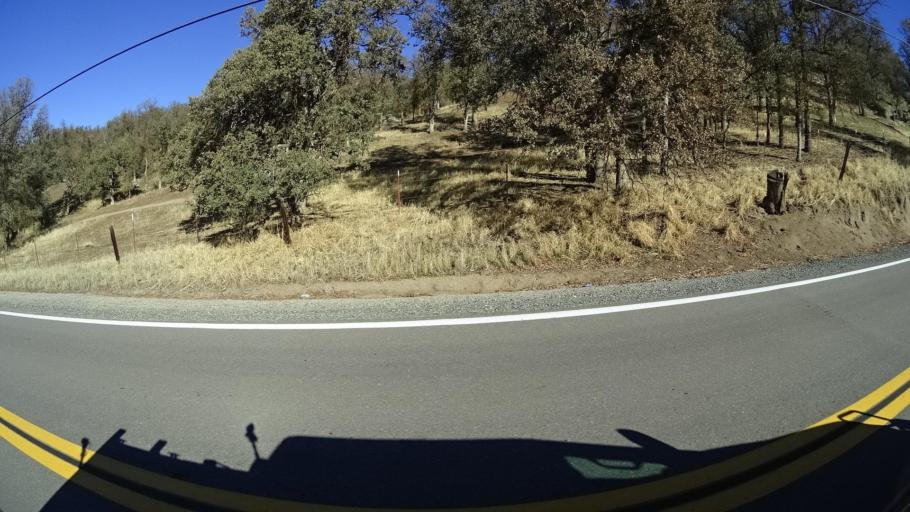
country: US
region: California
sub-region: Kern County
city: Alta Sierra
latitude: 35.7289
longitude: -118.7133
